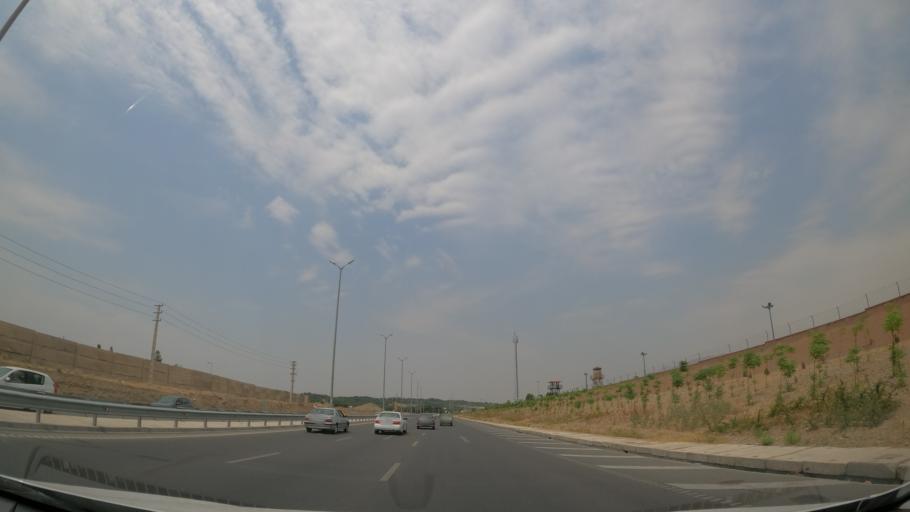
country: IR
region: Tehran
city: Shahr-e Qods
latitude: 35.7394
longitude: 51.2254
